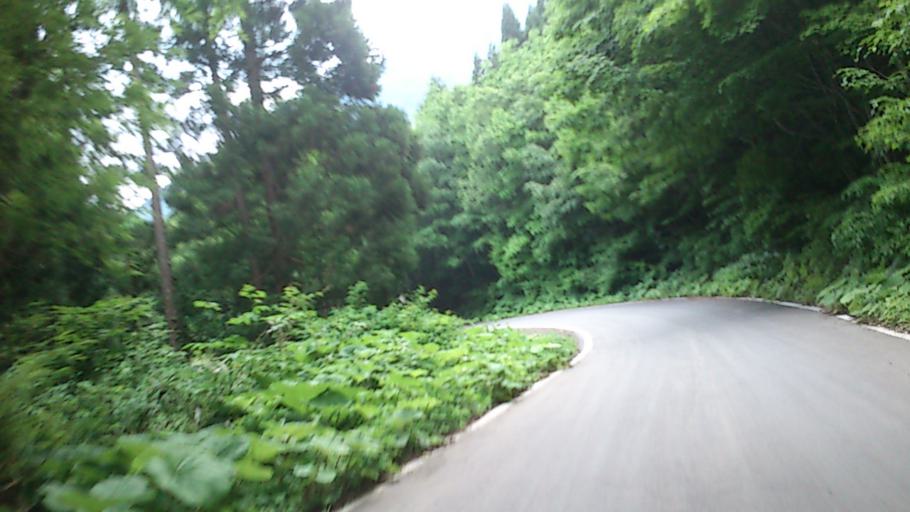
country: JP
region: Aomori
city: Hirosaki
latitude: 40.5479
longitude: 140.1823
